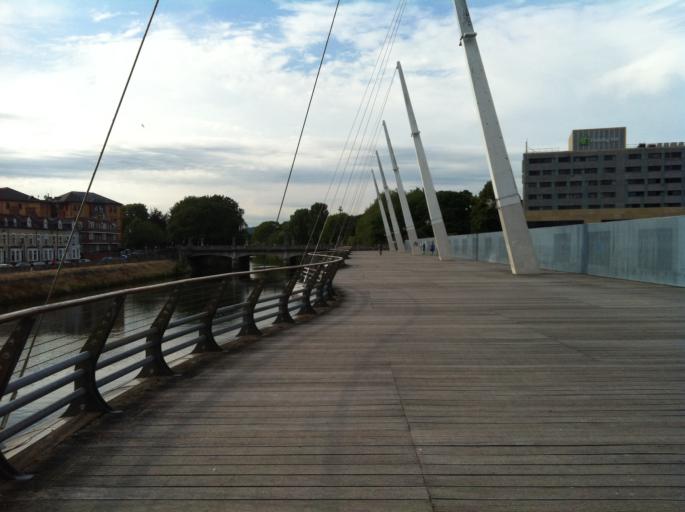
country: GB
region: Wales
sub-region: Cardiff
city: Cardiff
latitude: 51.4793
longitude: -3.1849
